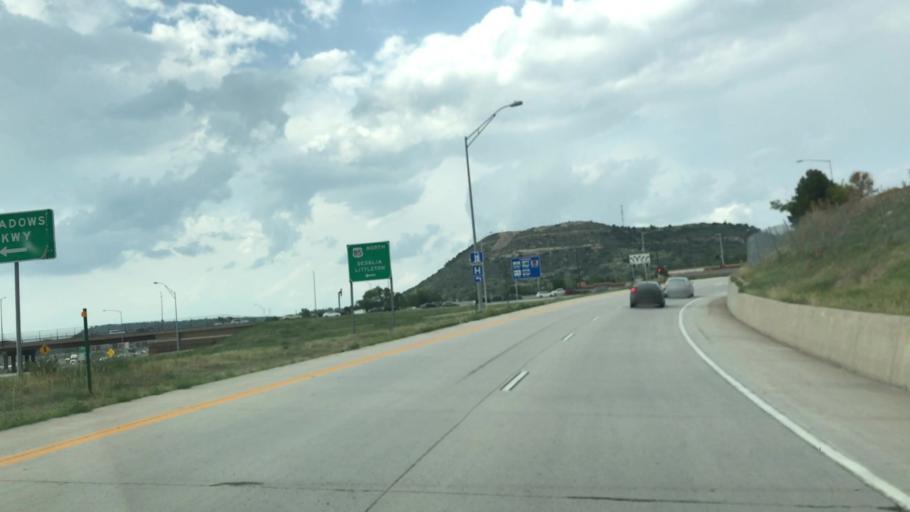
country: US
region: Colorado
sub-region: Douglas County
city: Castle Rock
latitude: 39.4110
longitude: -104.8662
